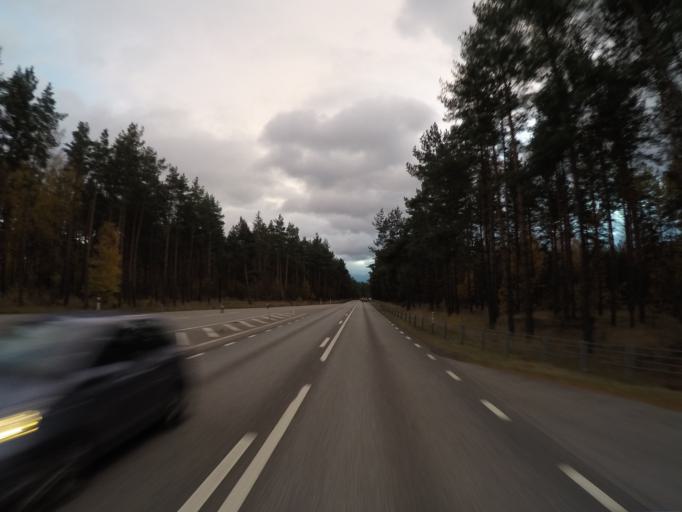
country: SE
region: Skane
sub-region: Kristianstads Kommun
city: Degeberga
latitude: 55.9097
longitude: 14.0730
